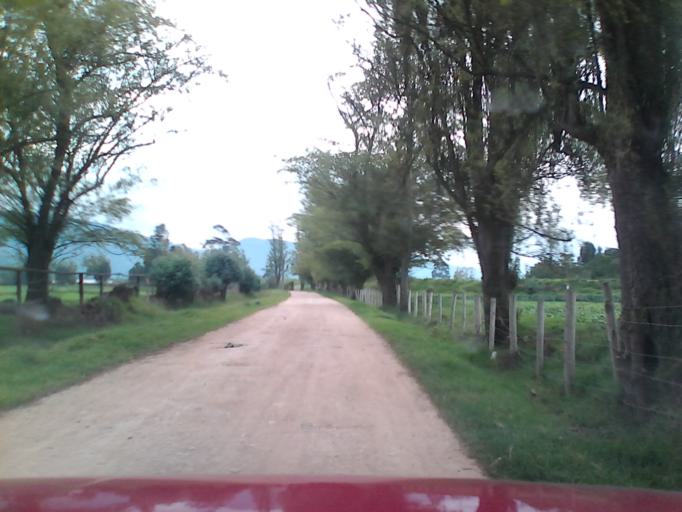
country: CO
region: Boyaca
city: Duitama
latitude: 5.8099
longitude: -73.0036
